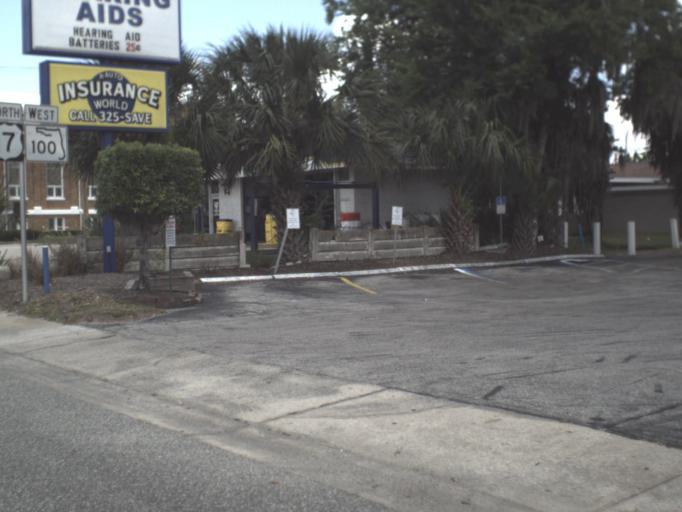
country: US
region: Florida
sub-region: Putnam County
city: Palatka
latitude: 29.6476
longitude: -81.6314
